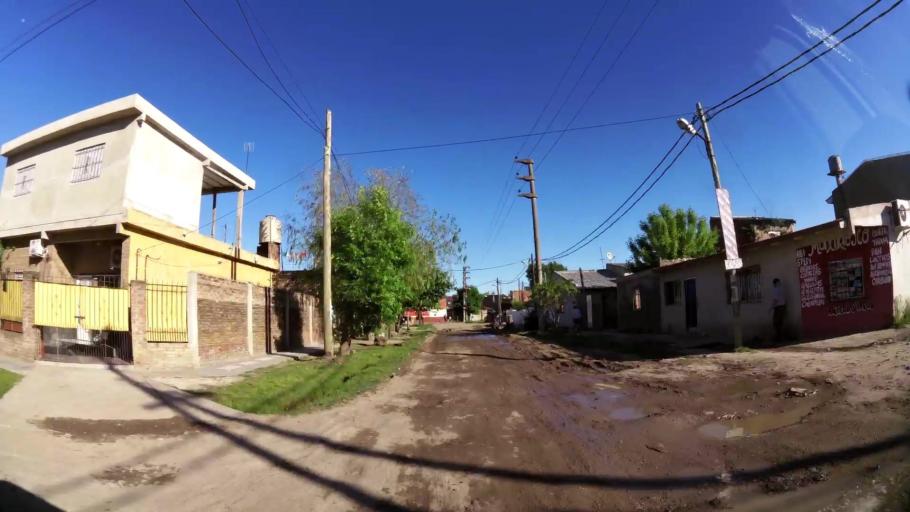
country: AR
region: Buenos Aires
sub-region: Partido de Quilmes
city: Quilmes
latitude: -34.7450
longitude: -58.3203
